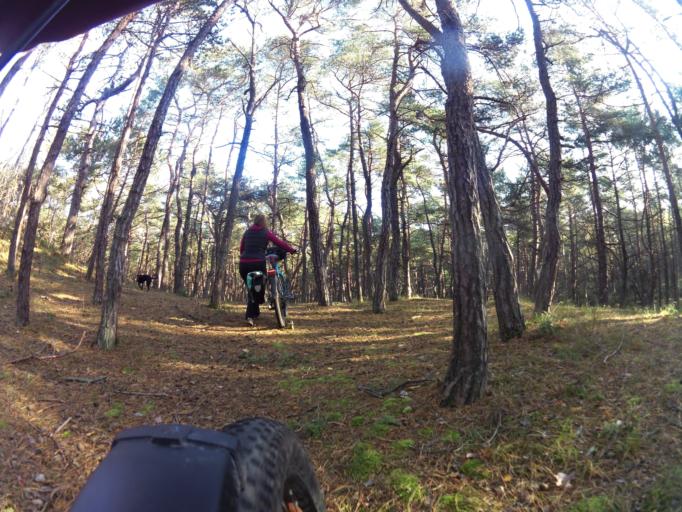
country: PL
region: Pomeranian Voivodeship
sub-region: Powiat pucki
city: Hel
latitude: 54.5989
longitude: 18.8134
